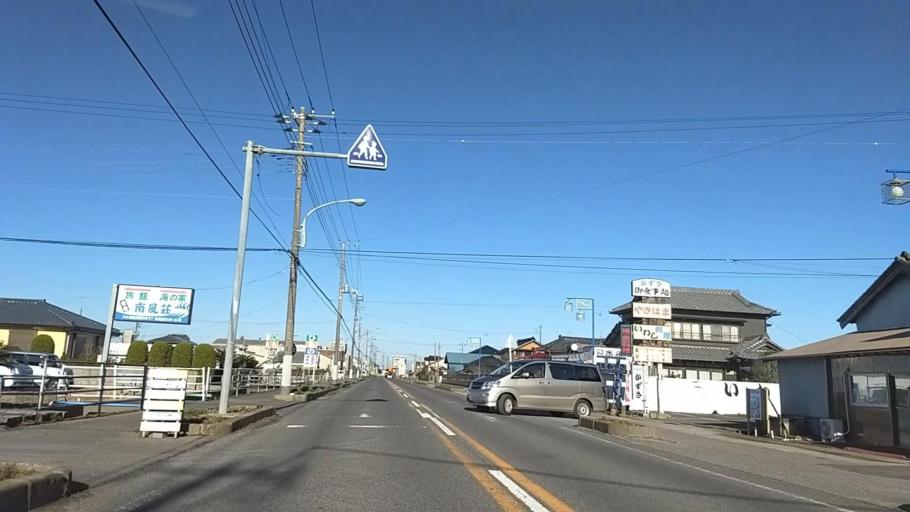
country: JP
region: Chiba
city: Naruto
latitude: 35.5335
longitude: 140.4515
